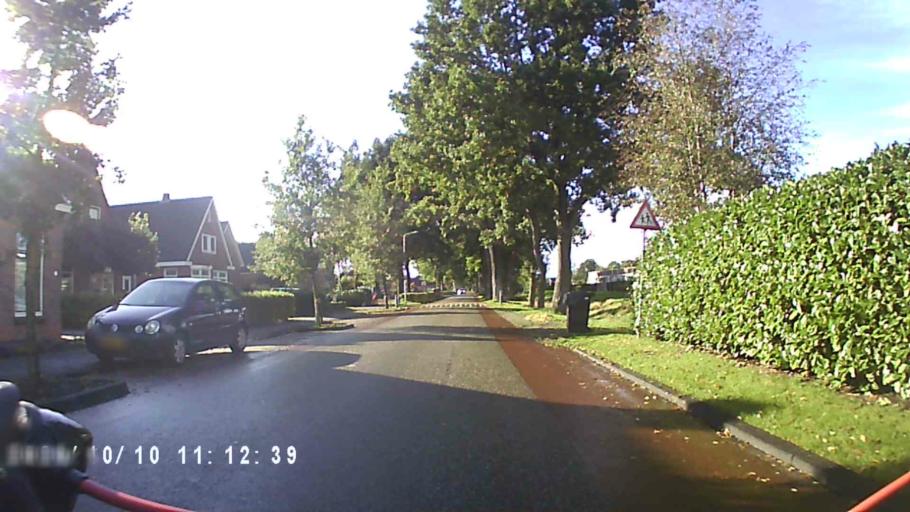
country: NL
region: Friesland
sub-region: Gemeente Smallingerland
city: Drachtstercompagnie
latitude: 53.1111
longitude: 6.2064
